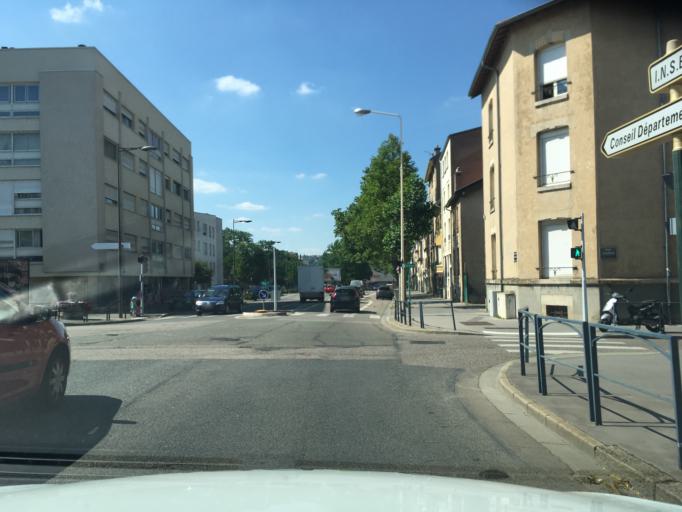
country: FR
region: Lorraine
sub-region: Departement de Meurthe-et-Moselle
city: Villers-les-Nancy
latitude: 48.6730
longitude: 6.1647
